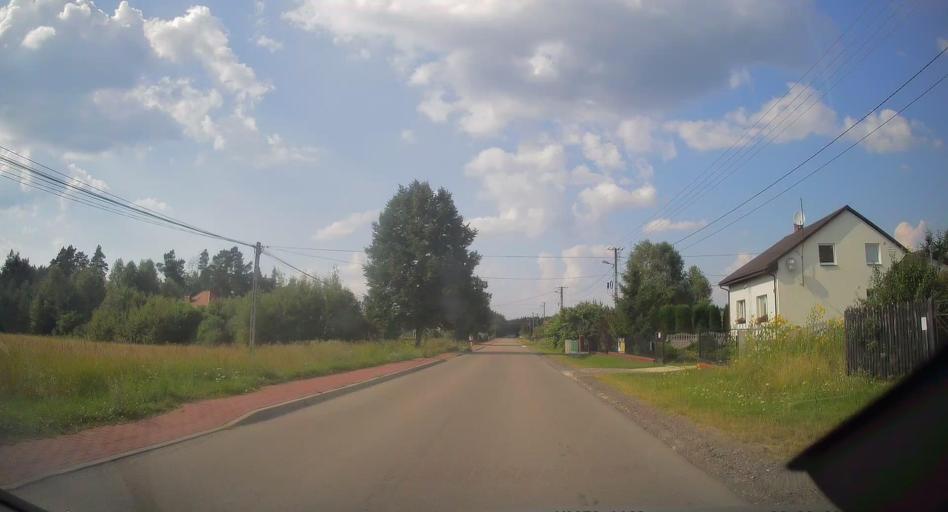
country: PL
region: Swietokrzyskie
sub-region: Powiat konecki
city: Radoszyce
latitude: 51.1178
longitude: 20.2603
